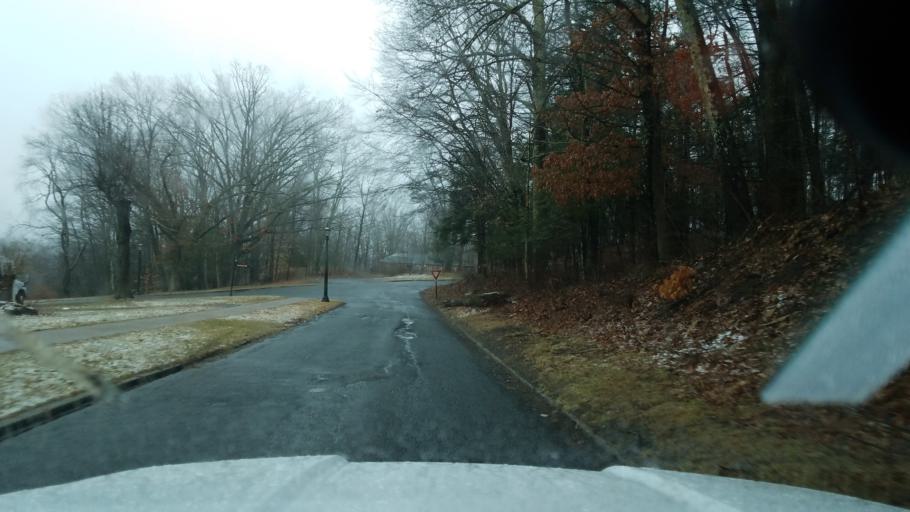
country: US
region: Connecticut
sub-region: New Haven County
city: Heritage Village
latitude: 41.4975
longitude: -73.2682
